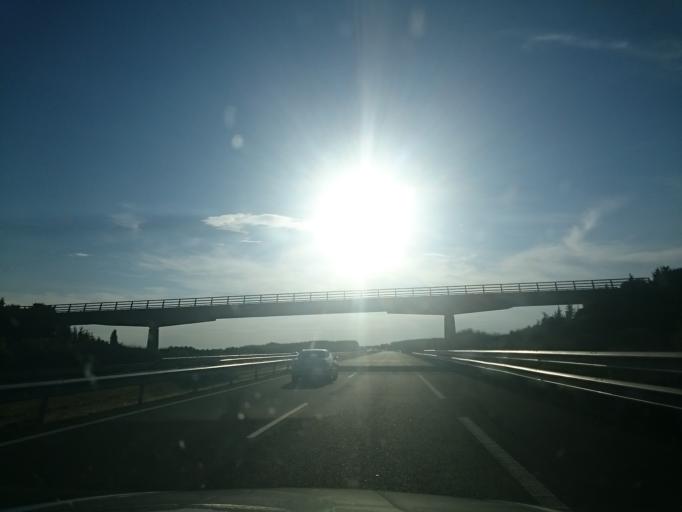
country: ES
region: Castille and Leon
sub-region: Provincia de Palencia
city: Bustillo del Paramo de Carrion
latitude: 42.3541
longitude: -4.7639
